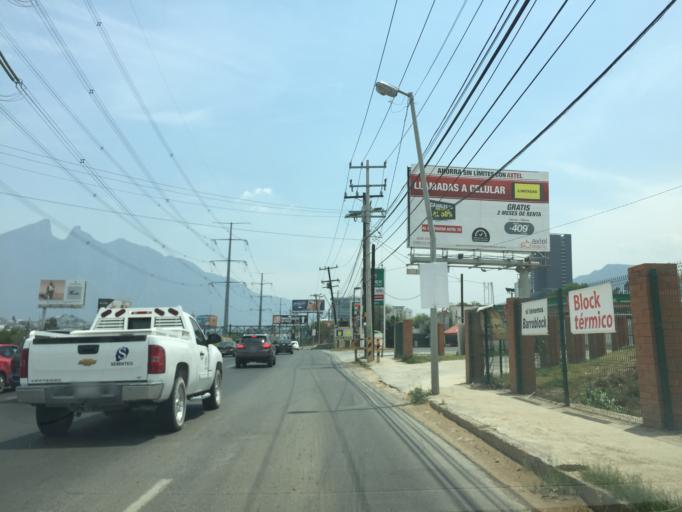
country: MX
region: Nuevo Leon
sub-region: Monterrey
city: Monterrey
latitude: 25.6346
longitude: -100.3070
